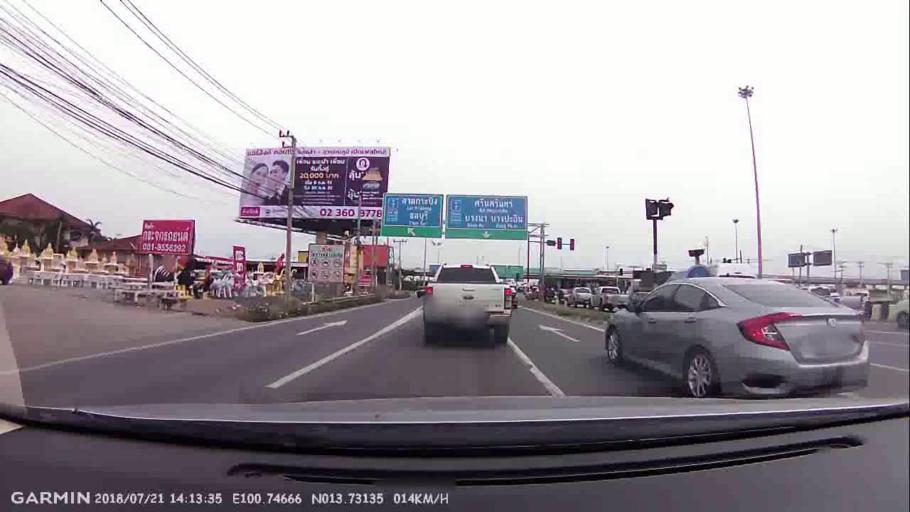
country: TH
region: Bangkok
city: Lat Krabang
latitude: 13.7313
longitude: 100.7467
